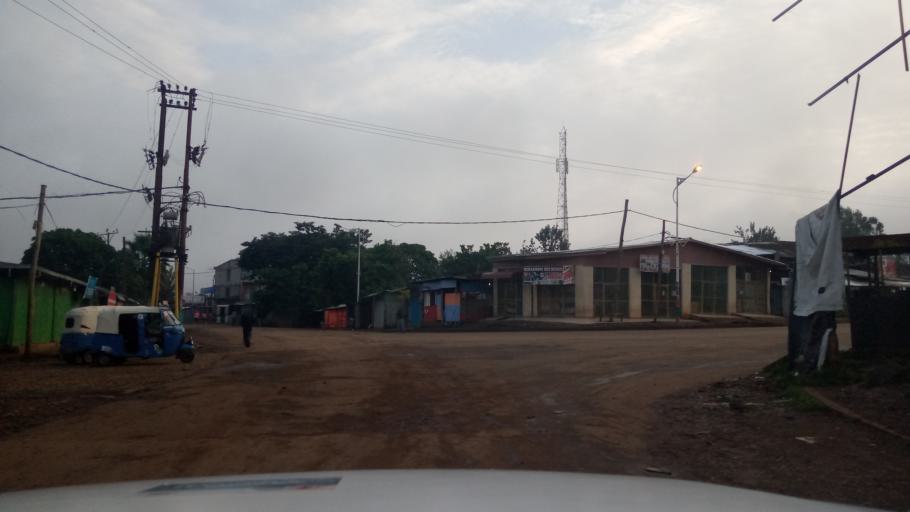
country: ET
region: Oromiya
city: Jima
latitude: 7.6833
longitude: 36.8498
